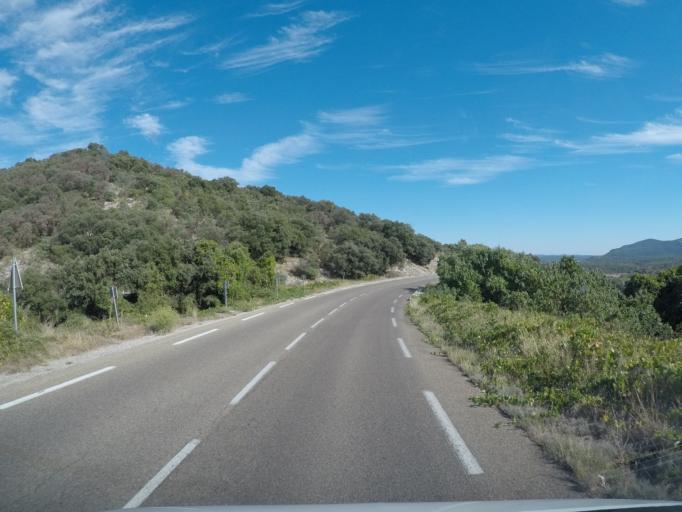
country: FR
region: Languedoc-Roussillon
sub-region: Departement du Gard
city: Saint-Hippolyte-du-Fort
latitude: 43.9607
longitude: 3.9027
